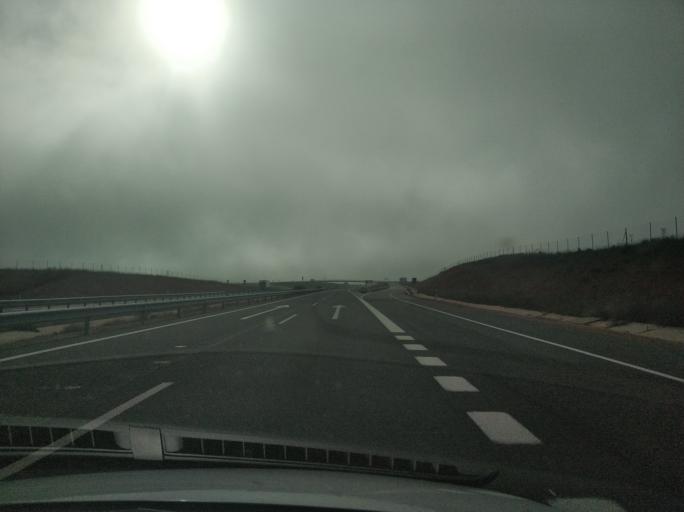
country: ES
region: Castille and Leon
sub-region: Provincia de Soria
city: Alcubilla de las Penas
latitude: 41.2653
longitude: -2.4741
